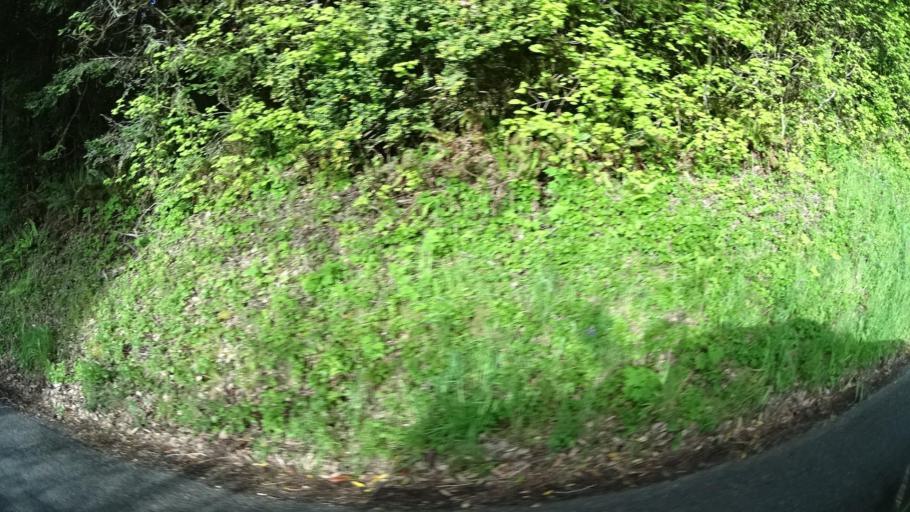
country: US
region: California
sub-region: Humboldt County
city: Blue Lake
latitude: 40.8788
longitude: -124.0146
